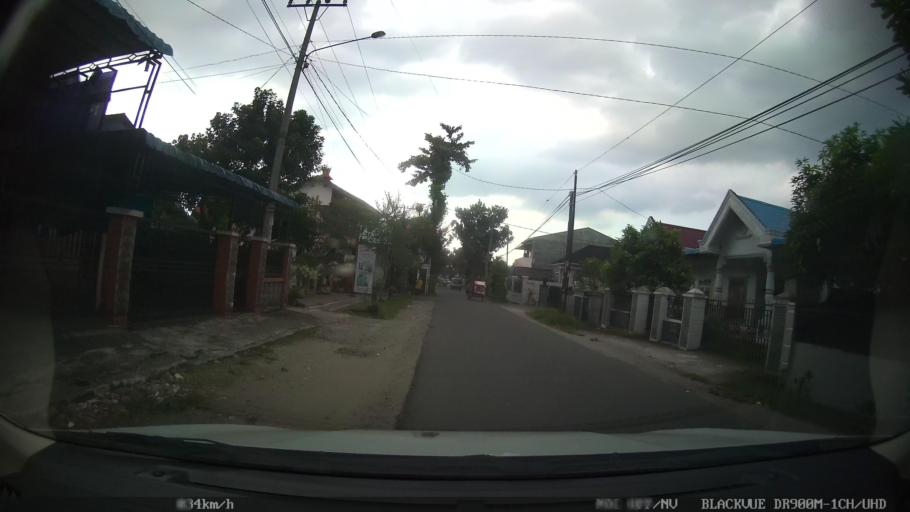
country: ID
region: North Sumatra
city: Sunggal
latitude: 3.5208
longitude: 98.6185
